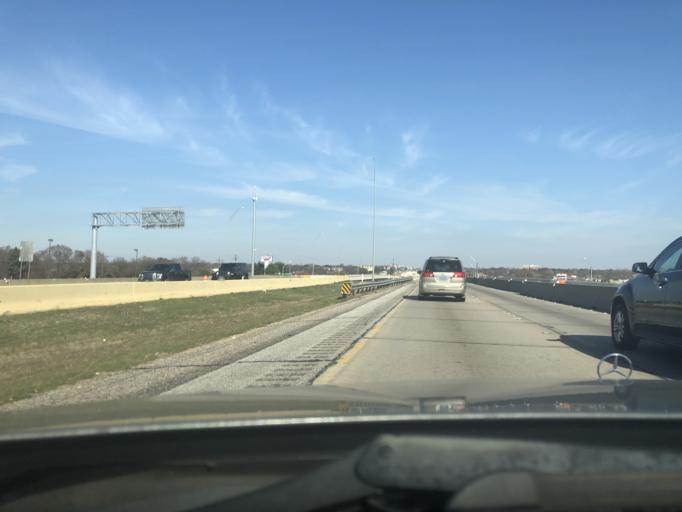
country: US
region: Texas
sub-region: Dallas County
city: Duncanville
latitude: 32.6241
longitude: -96.9094
